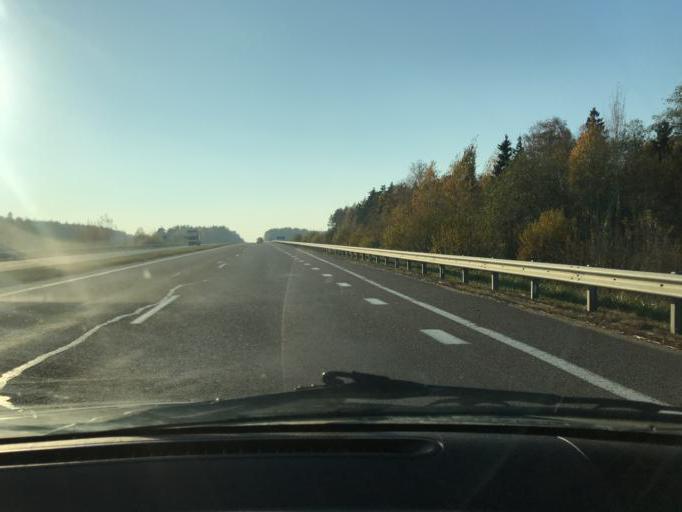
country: BY
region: Minsk
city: Loshnitsa
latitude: 54.2970
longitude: 28.9105
